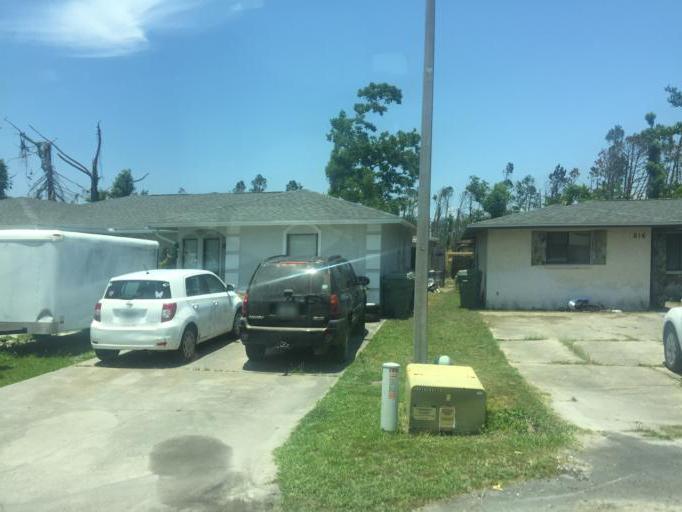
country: US
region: Florida
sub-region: Bay County
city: Lynn Haven
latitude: 30.2201
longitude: -85.6582
